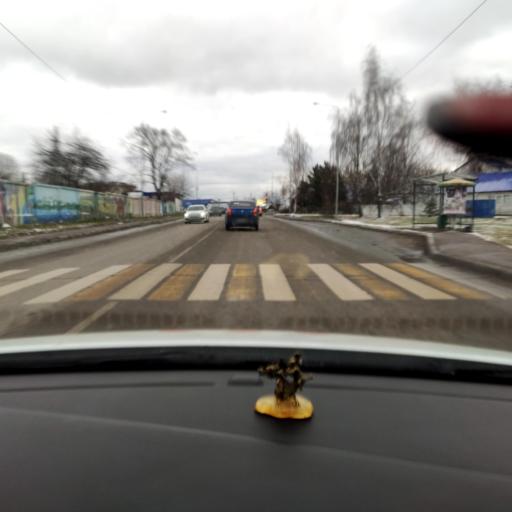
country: RU
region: Tatarstan
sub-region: Zelenodol'skiy Rayon
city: Zelenodolsk
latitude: 55.8461
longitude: 48.5510
